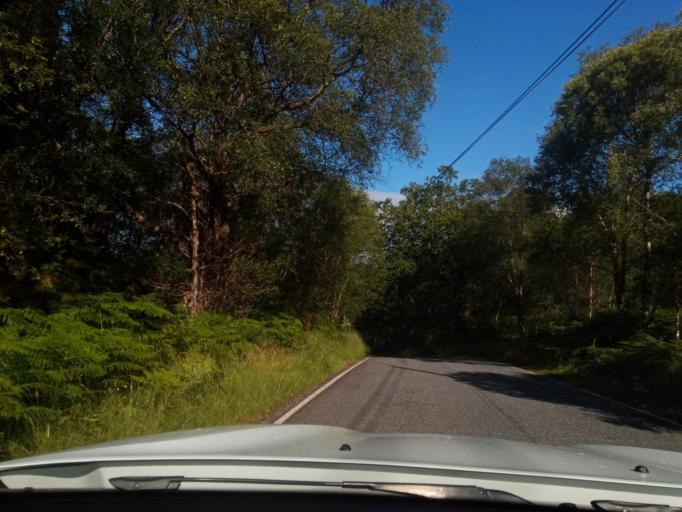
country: GB
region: Scotland
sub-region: Argyll and Bute
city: Isle Of Mull
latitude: 56.6871
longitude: -5.6595
